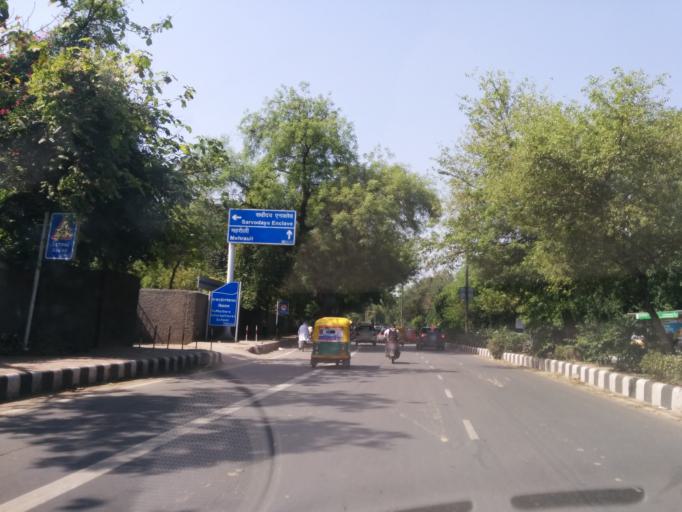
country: IN
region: NCT
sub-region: New Delhi
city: New Delhi
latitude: 28.5413
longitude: 77.1998
